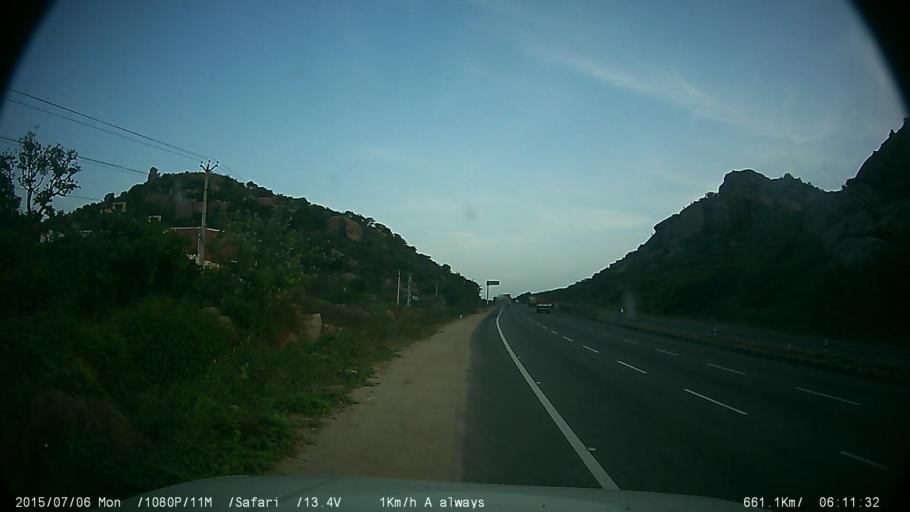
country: IN
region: Tamil Nadu
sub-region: Krishnagiri
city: Kelamangalam
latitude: 12.6559
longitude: 78.0228
